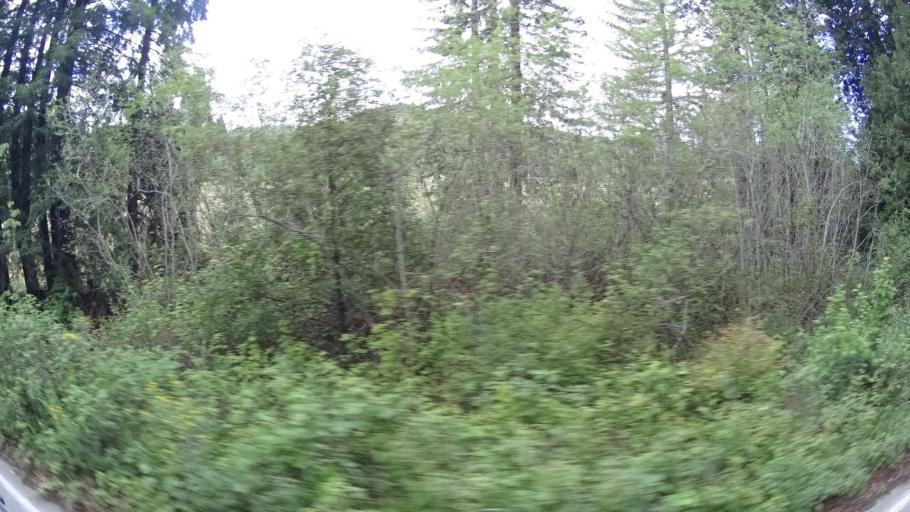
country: US
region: California
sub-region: Humboldt County
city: Blue Lake
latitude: 40.8683
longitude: -123.9695
